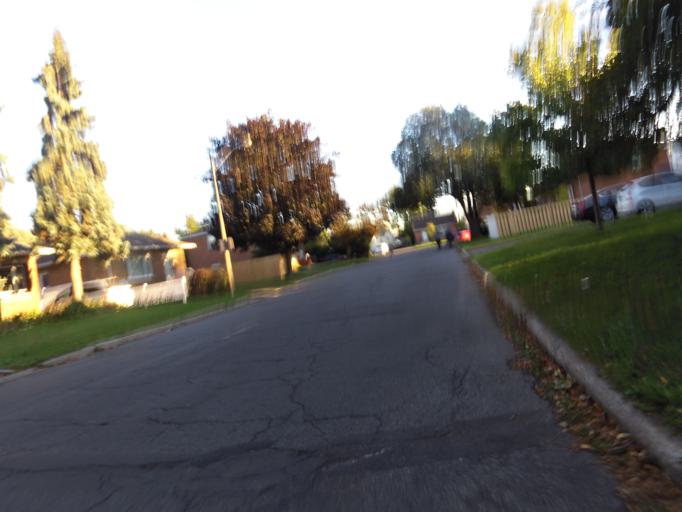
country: CA
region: Ontario
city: Ottawa
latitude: 45.4290
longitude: -75.6502
